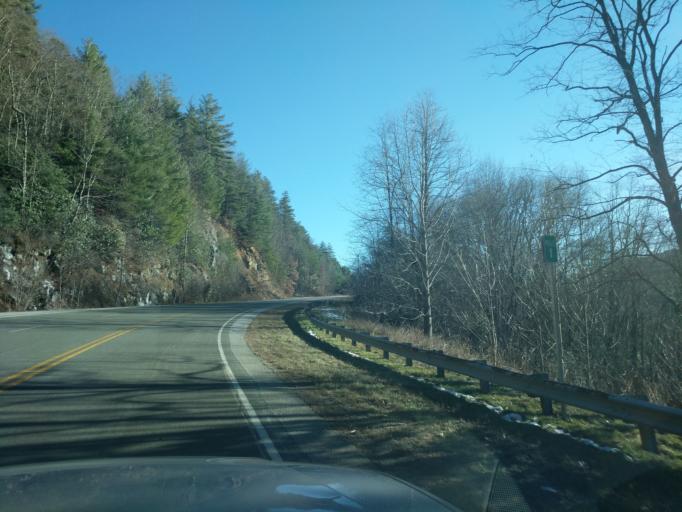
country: US
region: Georgia
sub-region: Towns County
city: Hiawassee
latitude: 34.9015
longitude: -83.6092
